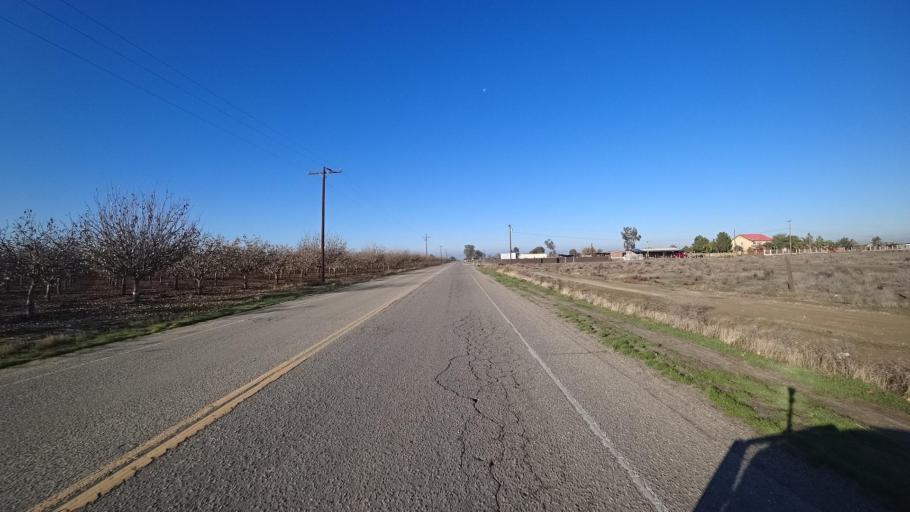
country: US
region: California
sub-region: Kern County
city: Delano
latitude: 35.7758
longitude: -119.3310
